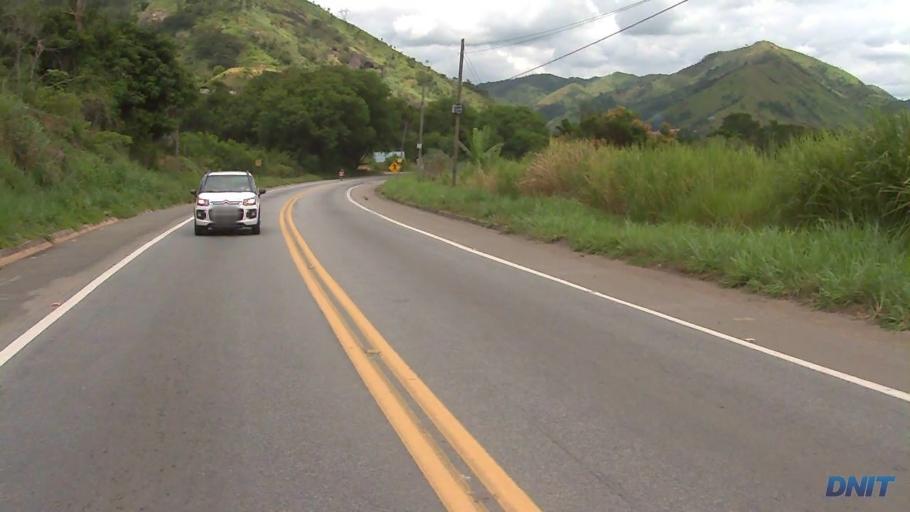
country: BR
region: Minas Gerais
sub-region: Timoteo
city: Timoteo
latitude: -19.5579
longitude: -42.7102
